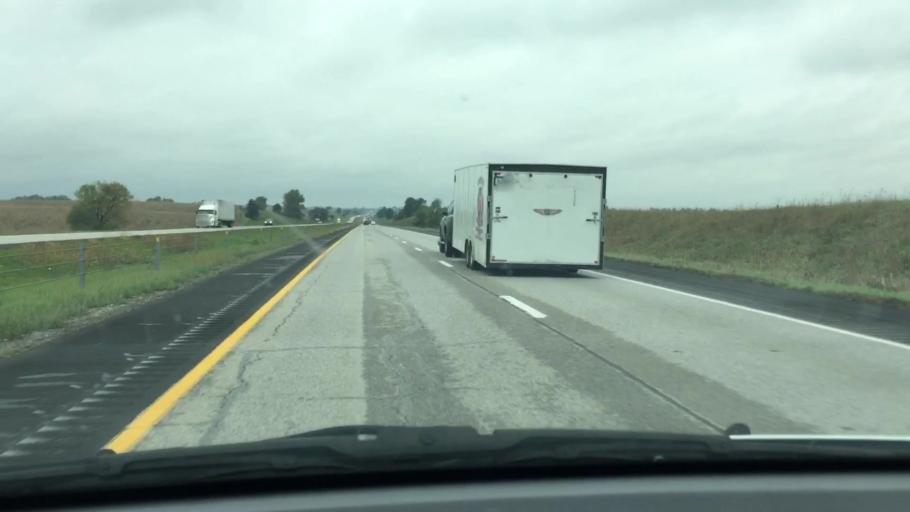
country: US
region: Iowa
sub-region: Iowa County
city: Williamsburg
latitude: 41.6873
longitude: -91.8599
